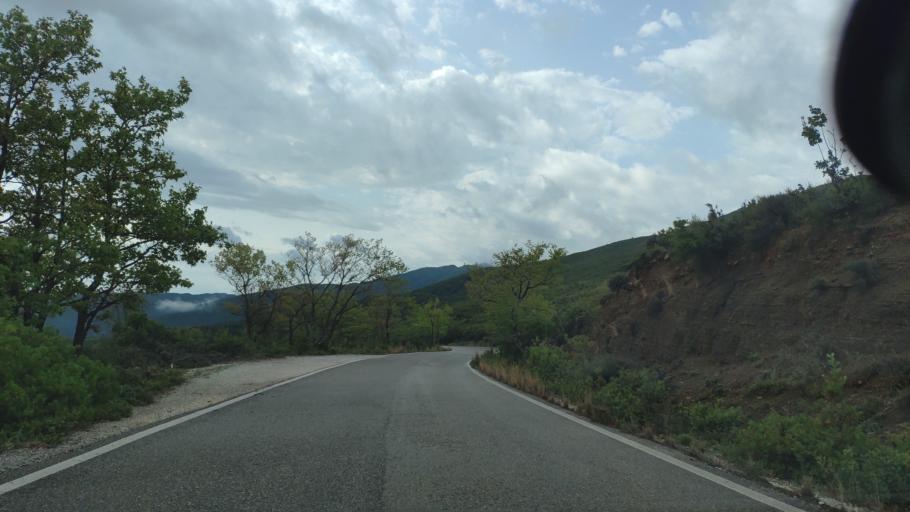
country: GR
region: West Greece
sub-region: Nomos Aitolias kai Akarnanias
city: Sardinia
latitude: 38.8457
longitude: 21.3168
